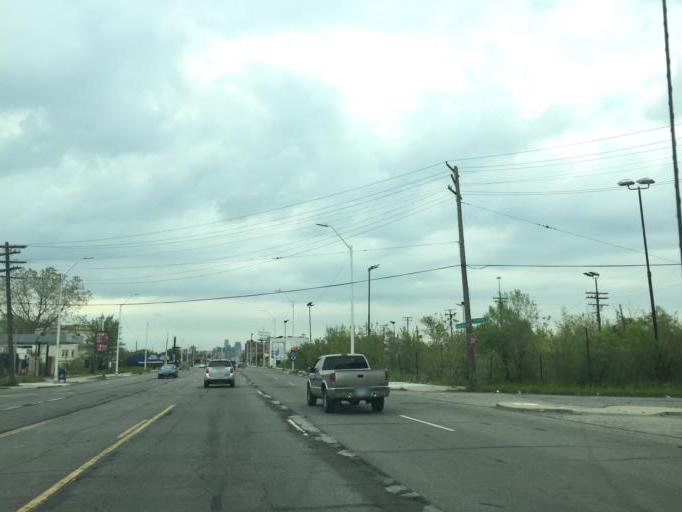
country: US
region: Michigan
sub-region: Wayne County
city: Highland Park
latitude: 42.3528
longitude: -83.0997
